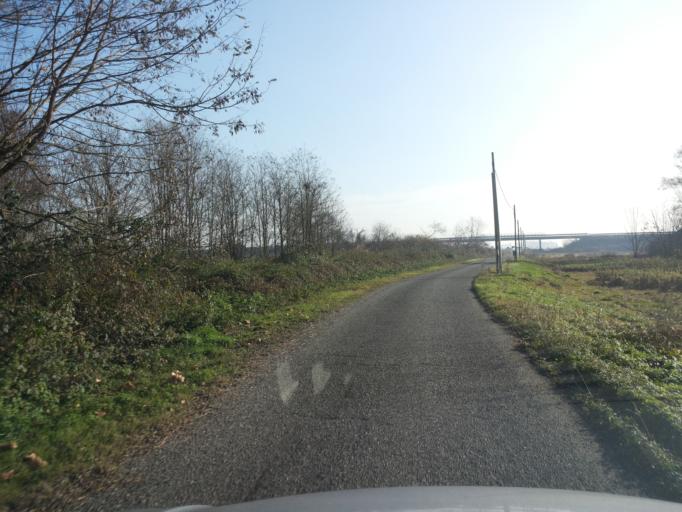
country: IT
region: Piedmont
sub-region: Provincia di Vercelli
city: Desana
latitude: 45.2699
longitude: 8.3645
